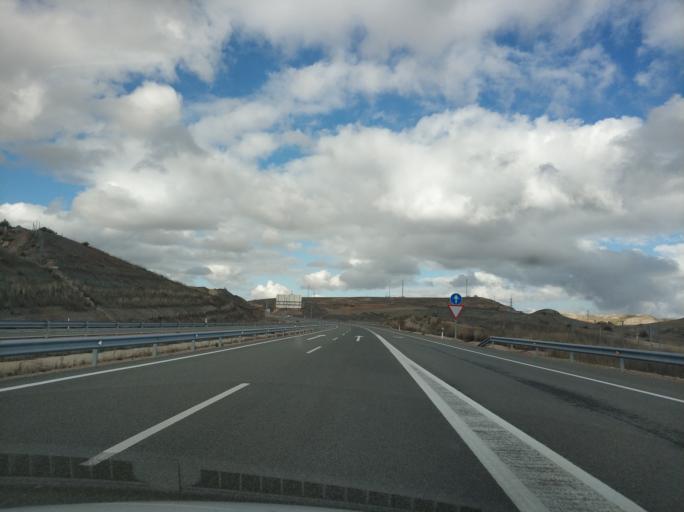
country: ES
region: Castille and Leon
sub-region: Provincia de Soria
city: Yelo
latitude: 41.2214
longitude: -2.4722
